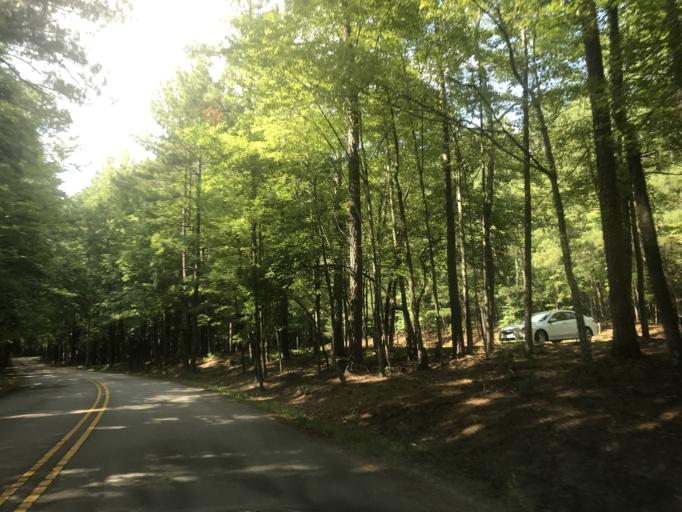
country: US
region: North Carolina
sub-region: Wake County
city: Morrisville
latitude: 35.8734
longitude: -78.7608
